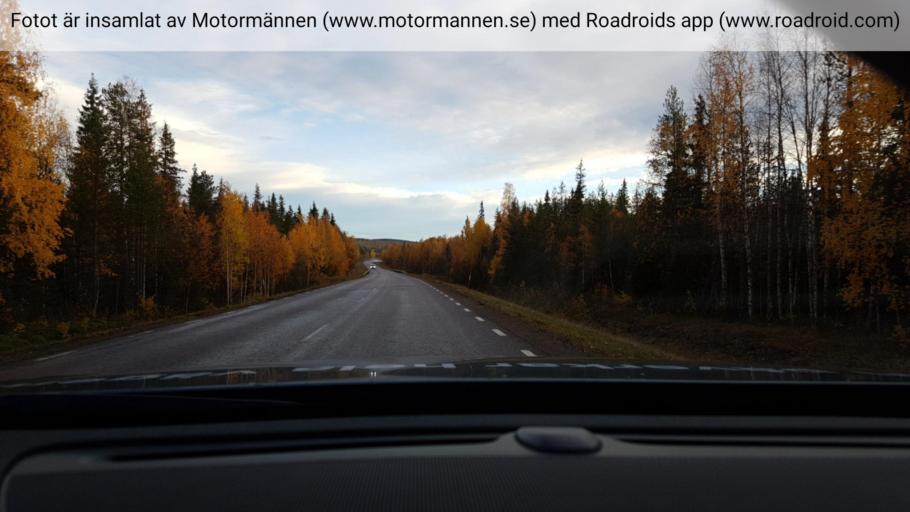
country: SE
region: Norrbotten
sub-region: Overkalix Kommun
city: OEverkalix
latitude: 66.8579
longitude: 22.7546
